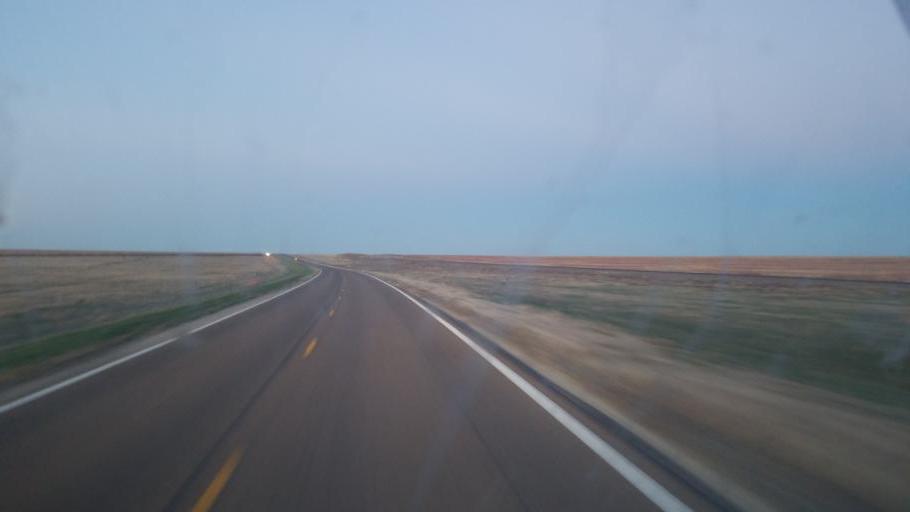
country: US
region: Kansas
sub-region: Wallace County
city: Sharon Springs
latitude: 39.0019
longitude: -101.3960
